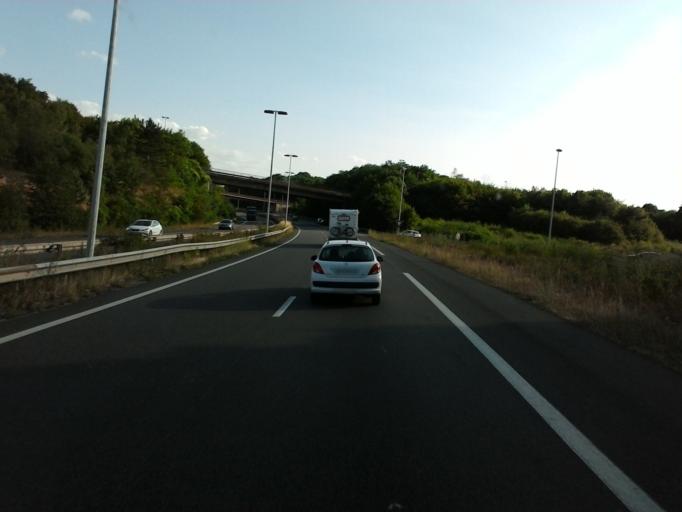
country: FR
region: Lorraine
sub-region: Departement de Meurthe-et-Moselle
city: Laxou
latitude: 48.6968
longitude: 6.1178
